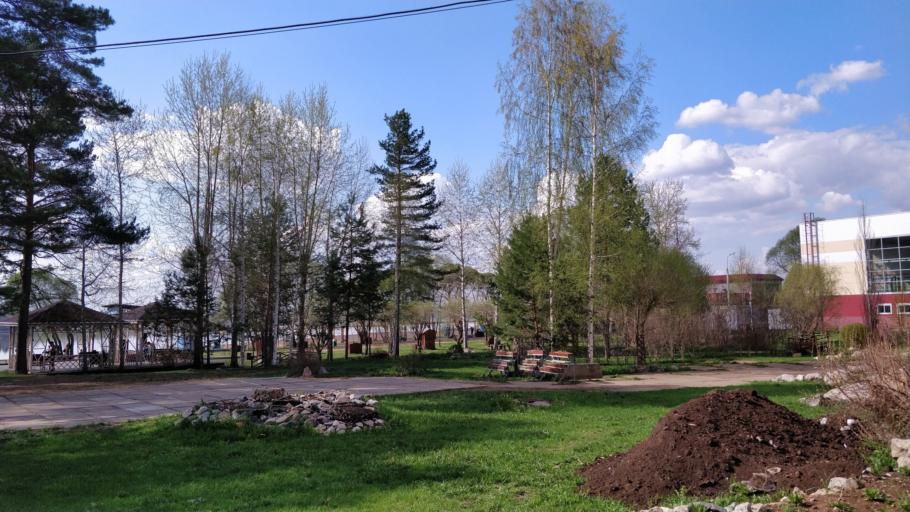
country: RU
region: Perm
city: Ust'-Kachka
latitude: 58.0116
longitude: 55.6708
